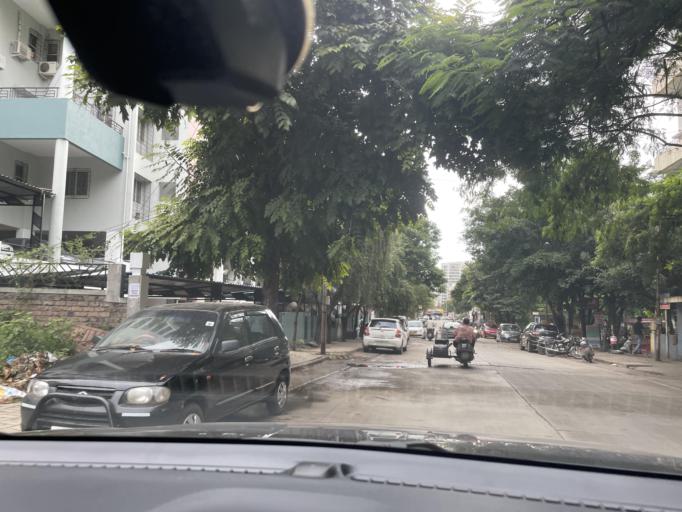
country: IN
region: Maharashtra
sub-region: Pune Division
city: Kharakvasla
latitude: 18.5112
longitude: 73.7793
